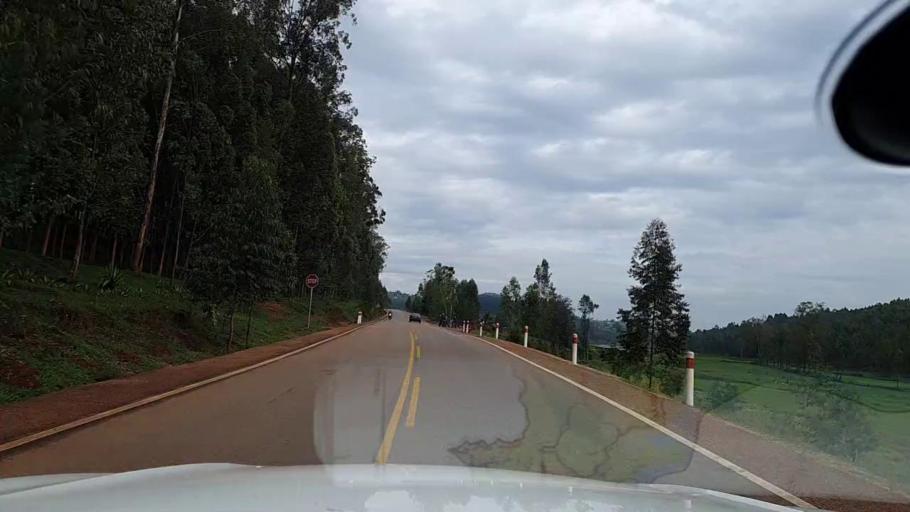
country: RW
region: Southern Province
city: Butare
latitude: -2.5624
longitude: 29.7220
